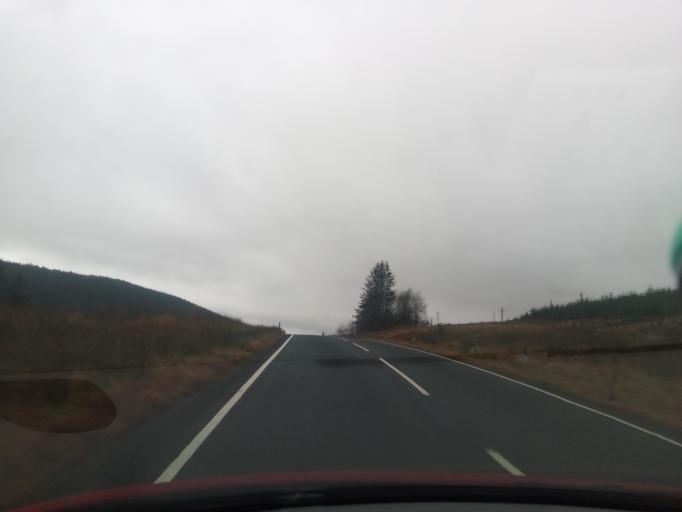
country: GB
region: Scotland
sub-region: The Scottish Borders
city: Hawick
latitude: 55.3062
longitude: -2.6599
